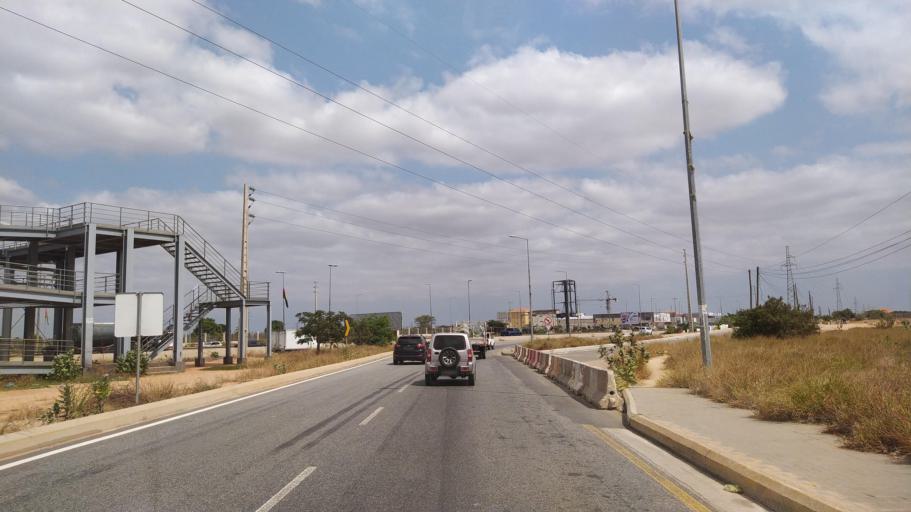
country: AO
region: Luanda
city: Luanda
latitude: -8.9728
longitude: 13.2523
